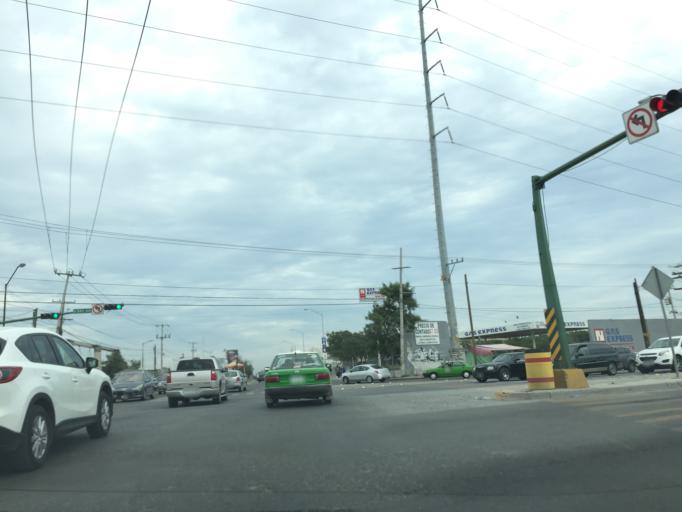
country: MX
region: Nuevo Leon
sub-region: Juarez
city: Valle de Juarez
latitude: 25.6667
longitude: -100.1737
